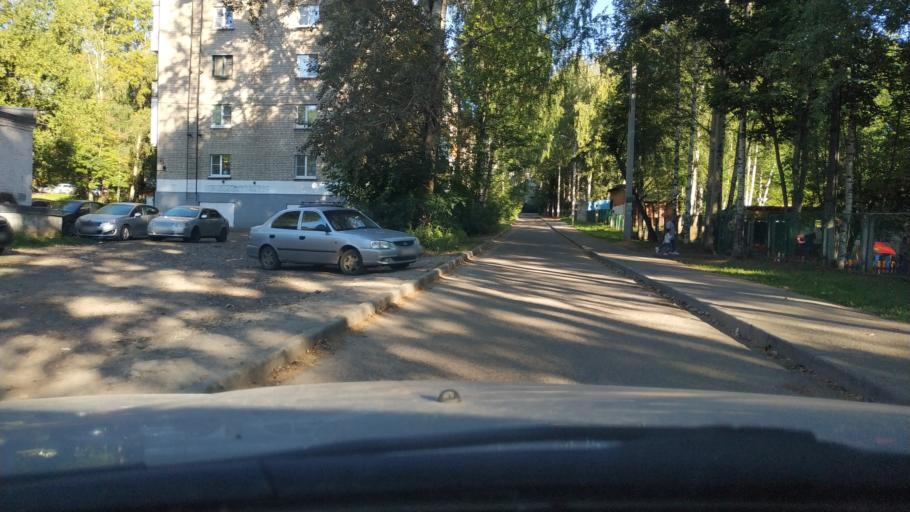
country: RU
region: Kostroma
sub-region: Kostromskoy Rayon
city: Kostroma
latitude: 57.7506
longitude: 40.9150
